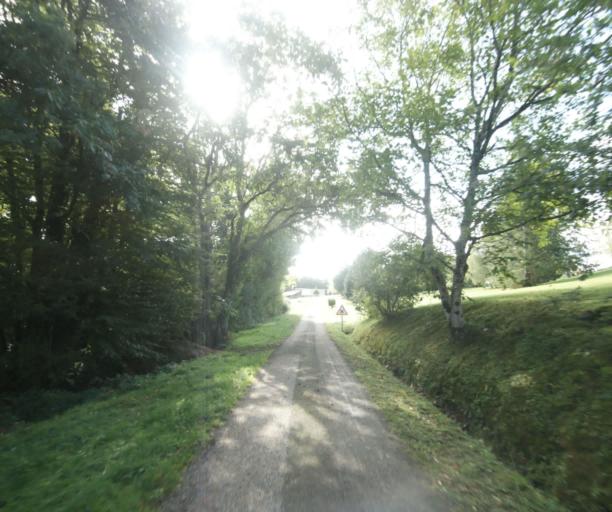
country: FR
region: Midi-Pyrenees
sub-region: Departement du Gers
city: Cazaubon
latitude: 43.8499
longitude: -0.0666
